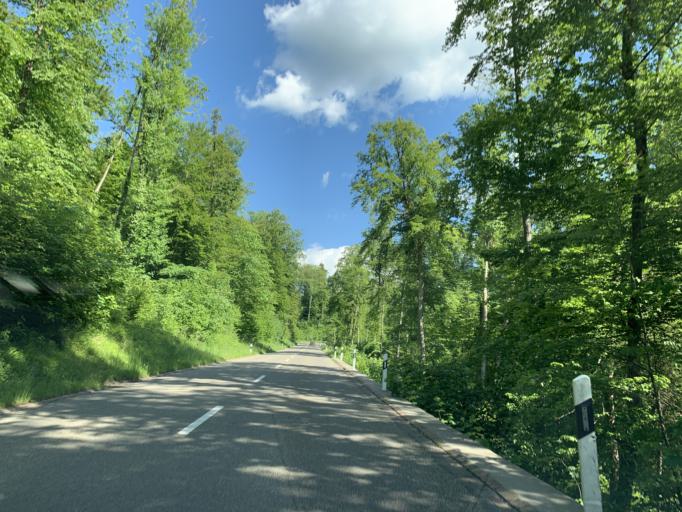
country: CH
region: Zurich
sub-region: Bezirk Pfaeffikon
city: Effretikon / Watt
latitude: 47.4403
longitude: 8.7101
